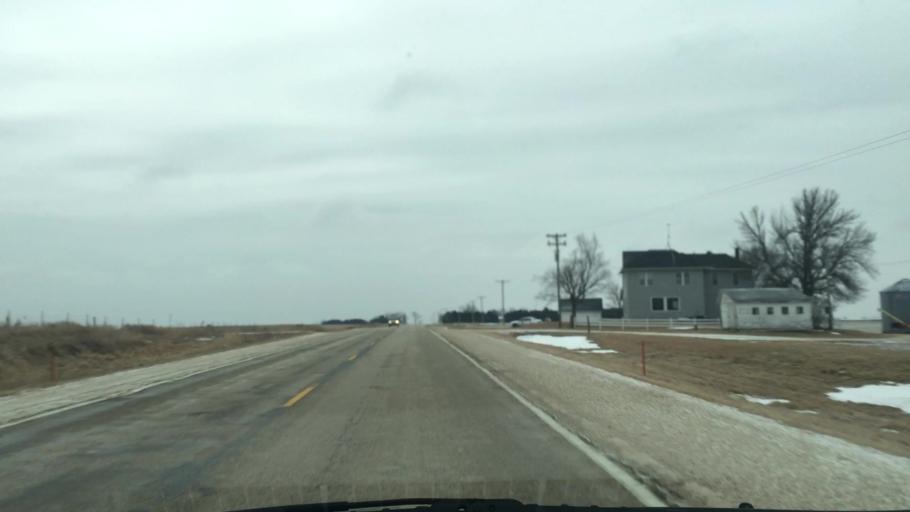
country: US
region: Iowa
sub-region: Fayette County
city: West Union
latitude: 43.0292
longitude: -91.8323
